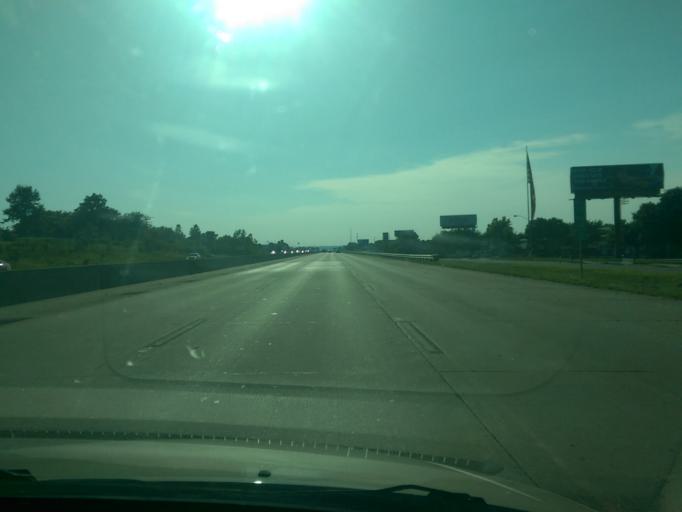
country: US
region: Missouri
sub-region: Jackson County
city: Blue Springs
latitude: 39.0322
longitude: -94.2870
